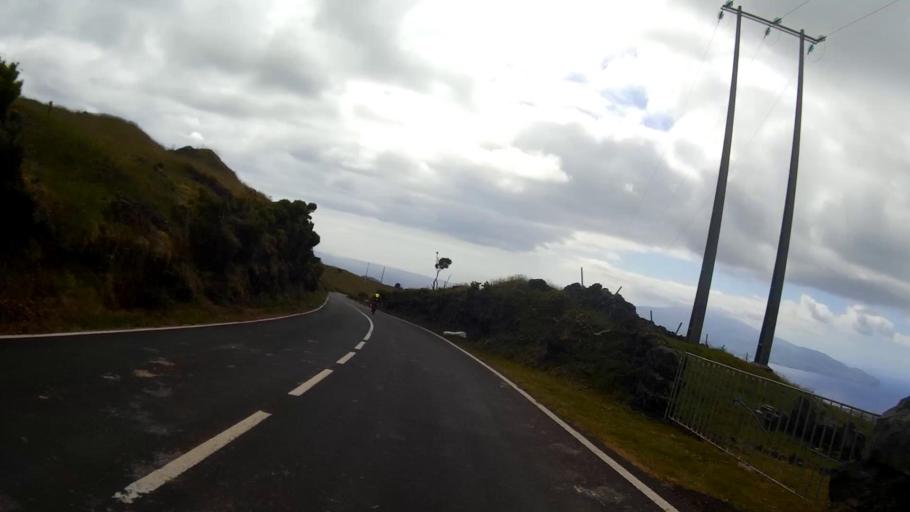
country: PT
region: Azores
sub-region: Madalena
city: Madalena
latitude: 38.4966
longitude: -28.4439
